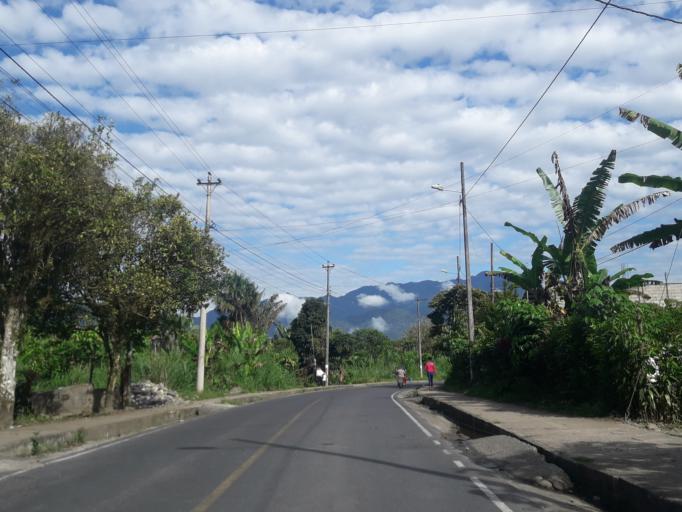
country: EC
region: Napo
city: Tena
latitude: -0.9844
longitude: -77.8400
